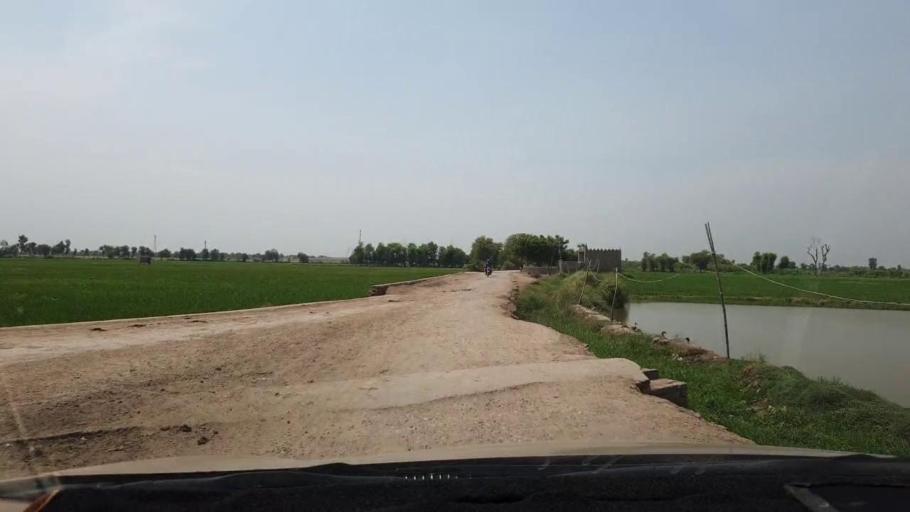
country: PK
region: Sindh
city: Naudero
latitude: 27.6297
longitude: 68.2739
